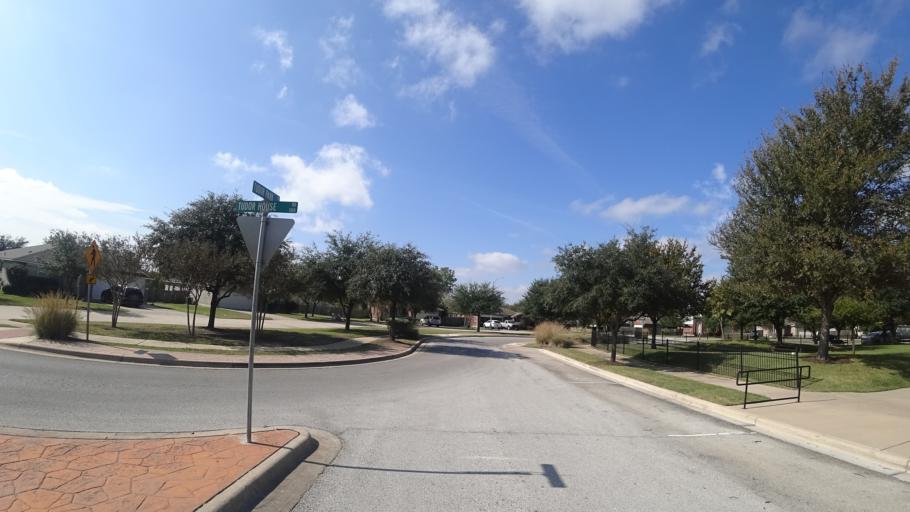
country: US
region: Texas
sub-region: Travis County
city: Pflugerville
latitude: 30.4195
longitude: -97.6393
